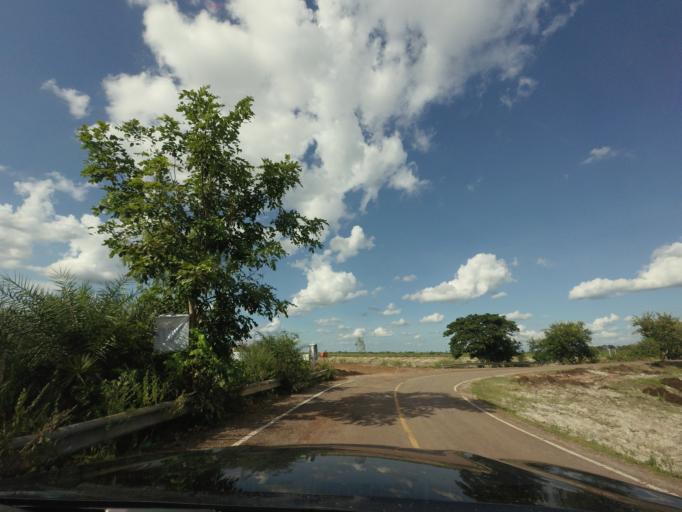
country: TH
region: Changwat Udon Thani
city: Ban Dung
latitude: 17.7502
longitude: 103.3580
